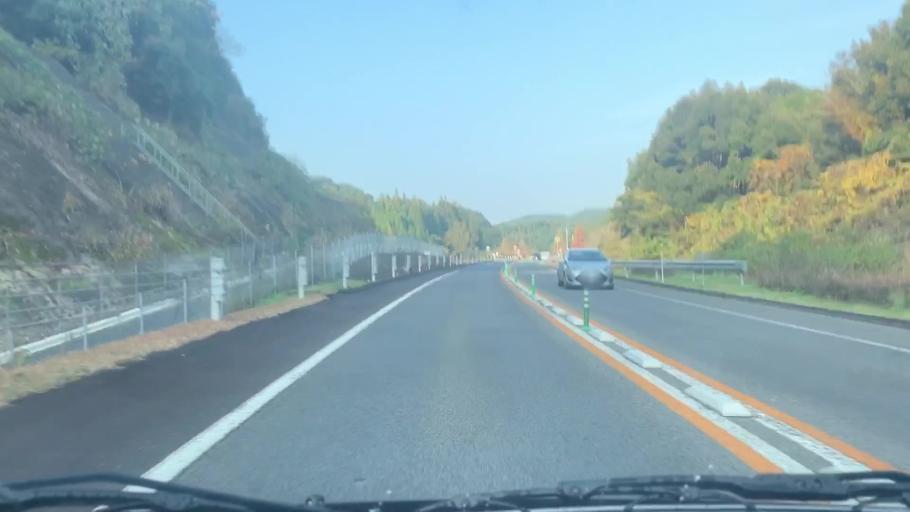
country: JP
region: Saga Prefecture
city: Ureshinomachi-shimojuku
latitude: 33.1432
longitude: 129.9728
